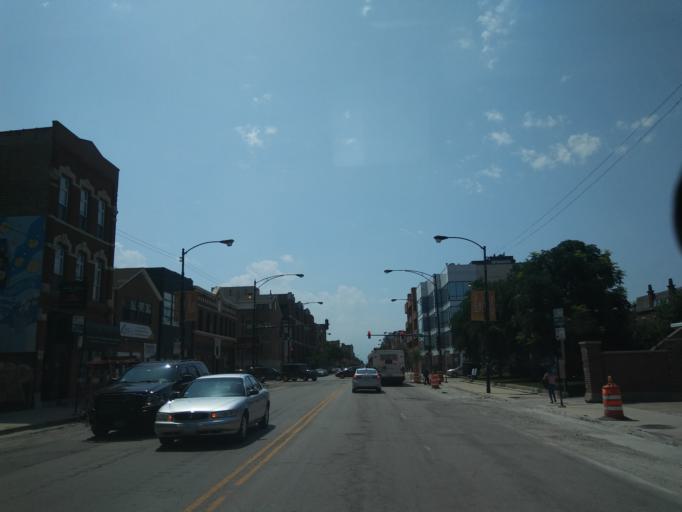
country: US
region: Illinois
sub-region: Cook County
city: Chicago
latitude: 41.8960
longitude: -87.6619
